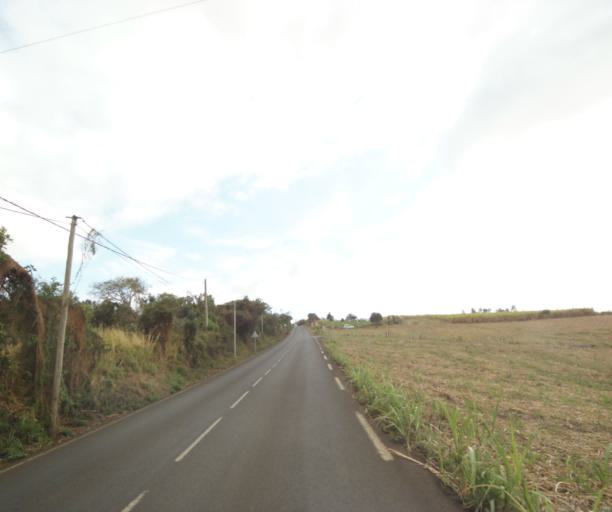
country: RE
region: Reunion
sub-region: Reunion
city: Trois-Bassins
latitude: -21.0658
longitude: 55.2788
